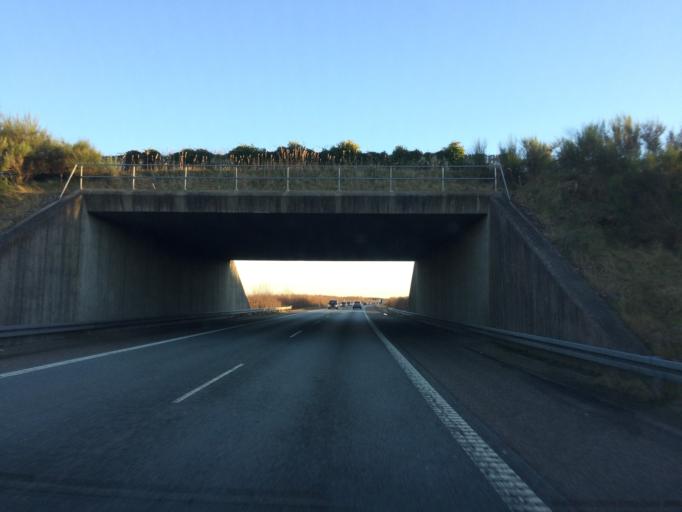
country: DK
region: Central Jutland
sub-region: Herning Kommune
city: Herning
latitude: 56.1779
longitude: 8.9815
